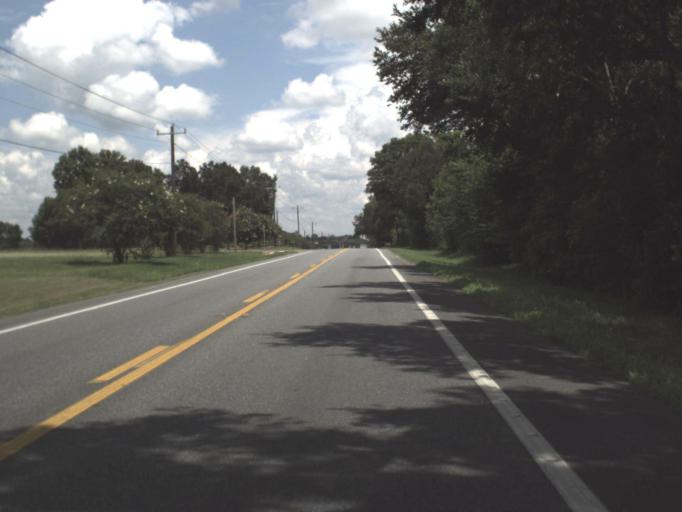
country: US
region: Florida
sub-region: Levy County
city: Williston
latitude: 29.3744
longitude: -82.4640
